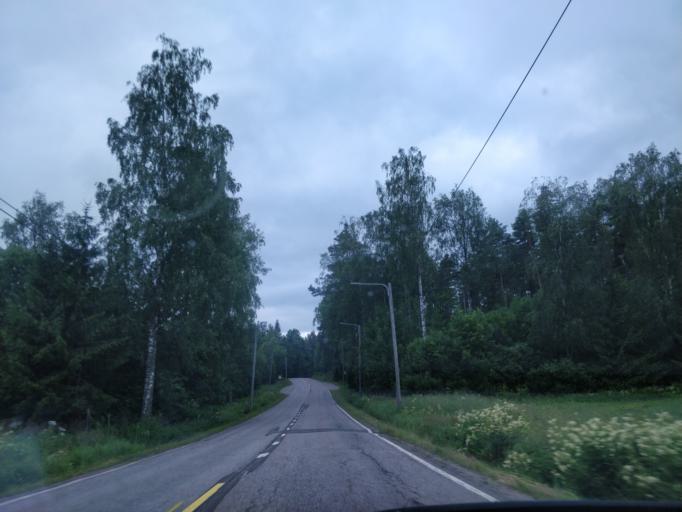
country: FI
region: Uusimaa
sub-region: Helsinki
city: Kauniainen
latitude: 60.3046
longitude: 24.7016
